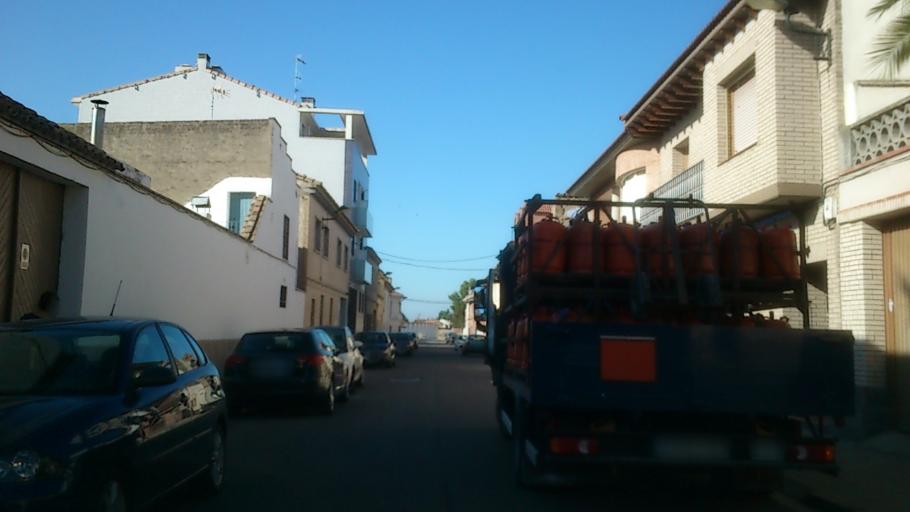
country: ES
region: Aragon
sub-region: Provincia de Zaragoza
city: Villanueva de Gallego
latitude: 41.7667
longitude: -0.8246
